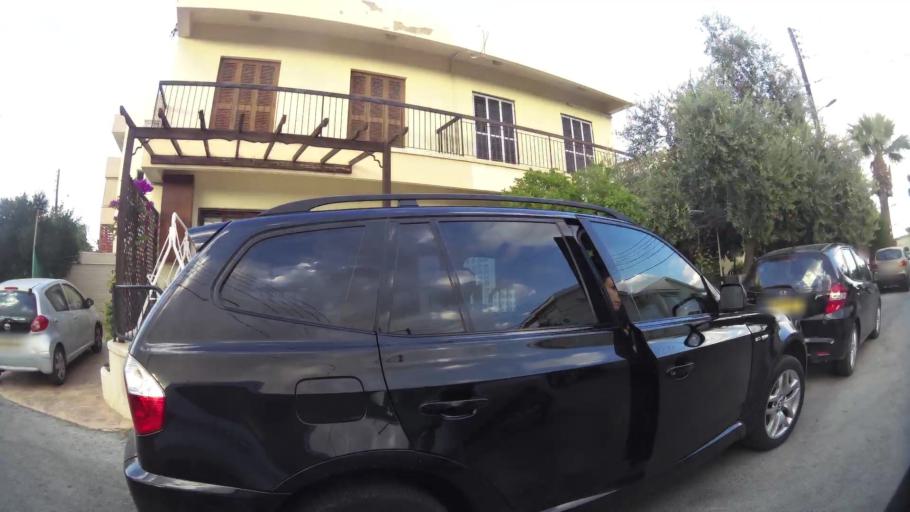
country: CY
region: Lefkosia
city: Tseri
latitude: 35.1193
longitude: 33.3123
